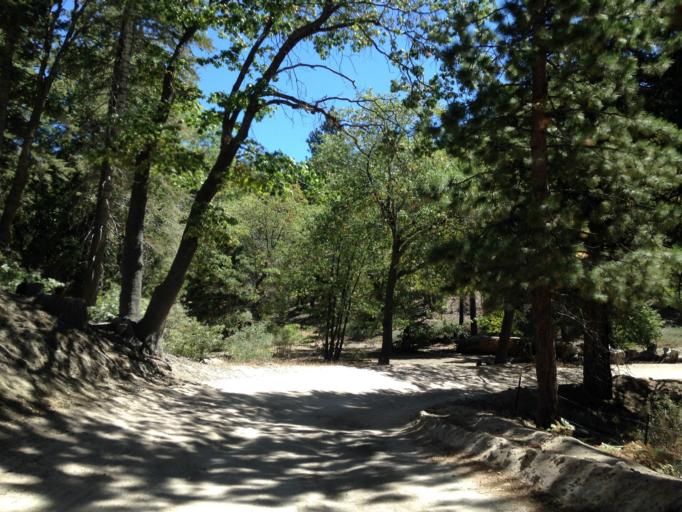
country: US
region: California
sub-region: San Bernardino County
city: Running Springs
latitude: 34.2450
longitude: -117.0855
